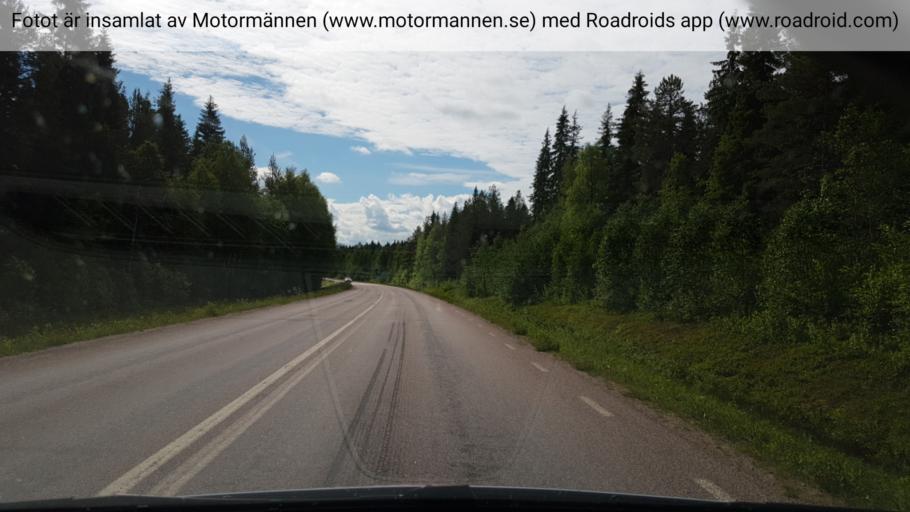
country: SE
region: Norrbotten
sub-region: Overtornea Kommun
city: OEvertornea
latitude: 66.4467
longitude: 23.6170
